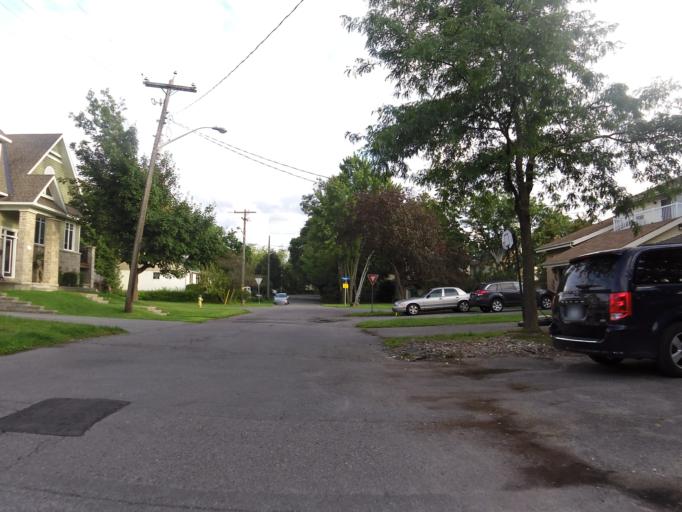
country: CA
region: Ontario
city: Ottawa
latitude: 45.3802
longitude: -75.7749
